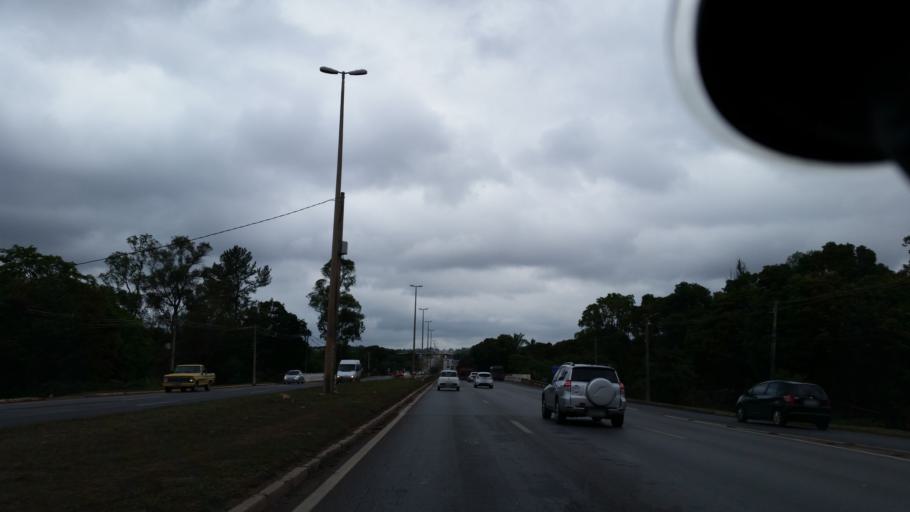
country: BR
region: Federal District
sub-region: Brasilia
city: Brasilia
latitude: -15.8644
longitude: -47.9572
